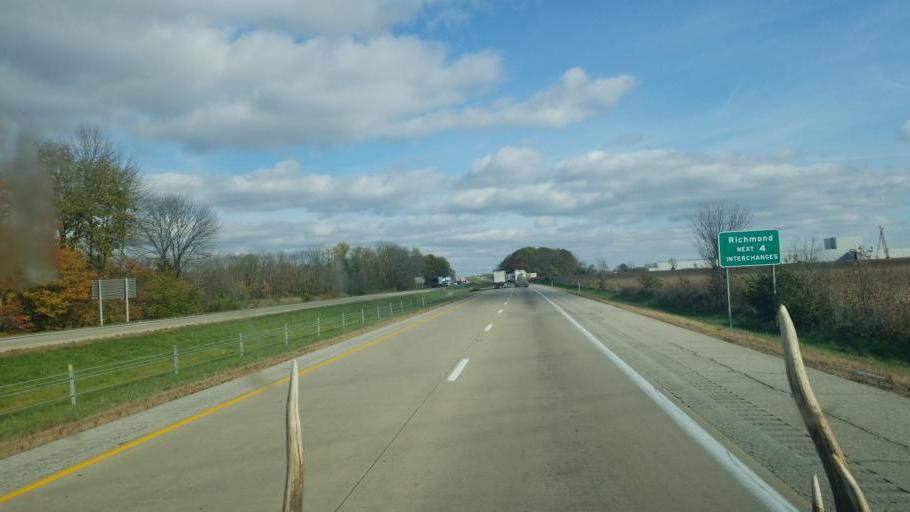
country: US
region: Indiana
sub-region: Wayne County
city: Centerville
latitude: 39.8599
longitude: -84.9753
